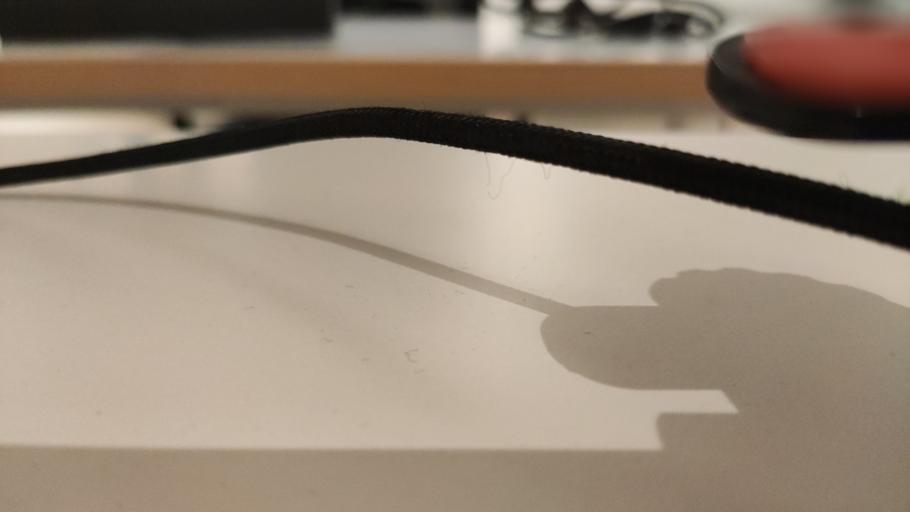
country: RU
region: Kaluga
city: Borovsk
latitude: 55.3570
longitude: 36.4250
